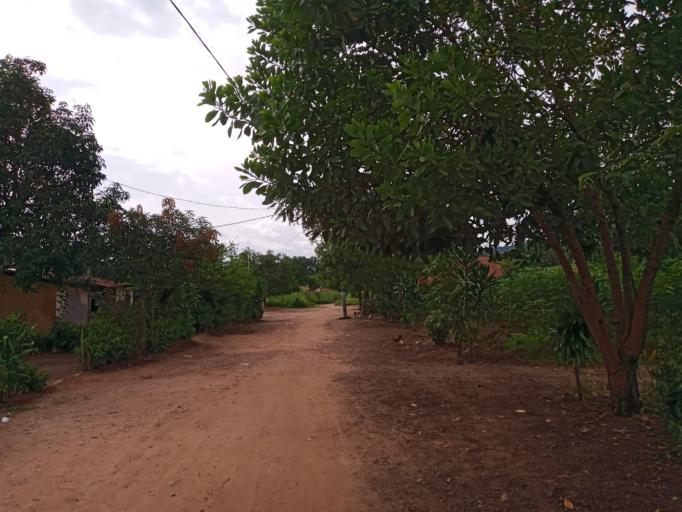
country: SL
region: Northern Province
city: Bumbuna
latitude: 9.0501
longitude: -11.7517
